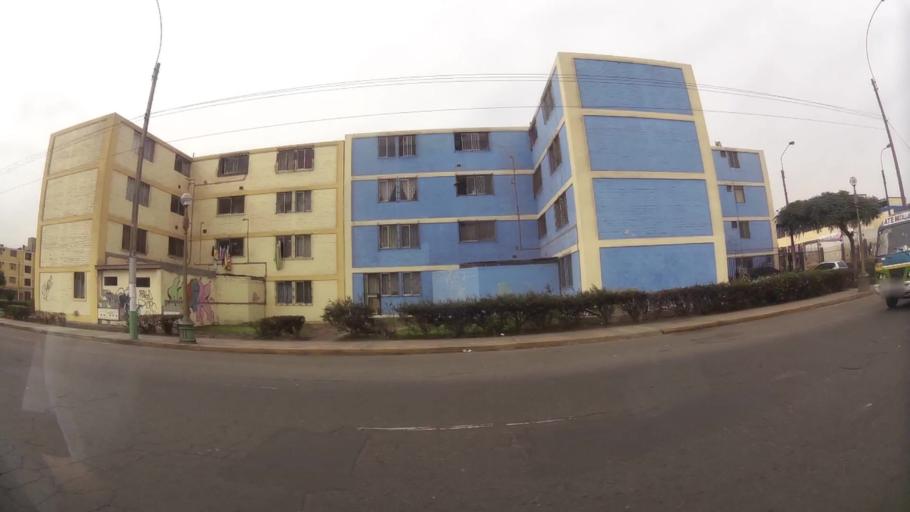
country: PE
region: Callao
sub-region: Callao
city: Callao
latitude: -12.0175
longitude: -77.1022
